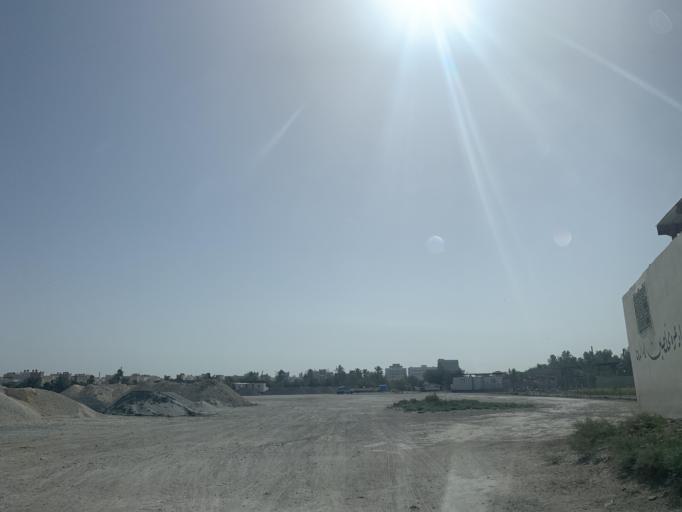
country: BH
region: Manama
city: Jidd Hafs
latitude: 26.2082
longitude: 50.5601
